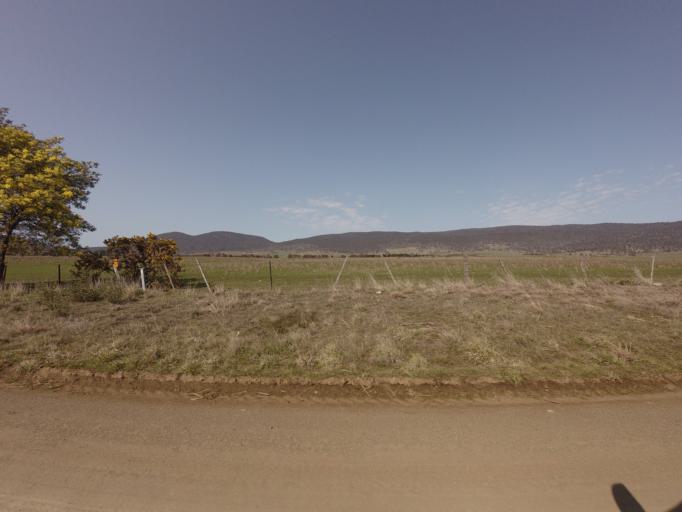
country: AU
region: Tasmania
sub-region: Break O'Day
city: St Helens
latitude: -41.8169
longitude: 147.9378
